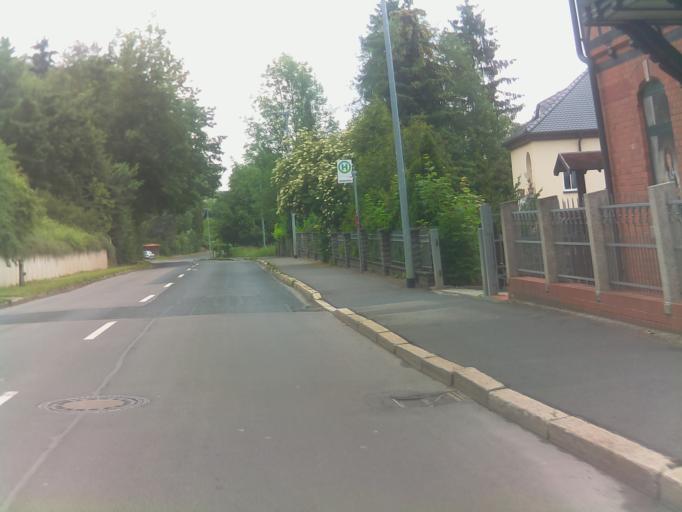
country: DE
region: Thuringia
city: Meiningen
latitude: 50.5784
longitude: 10.4074
